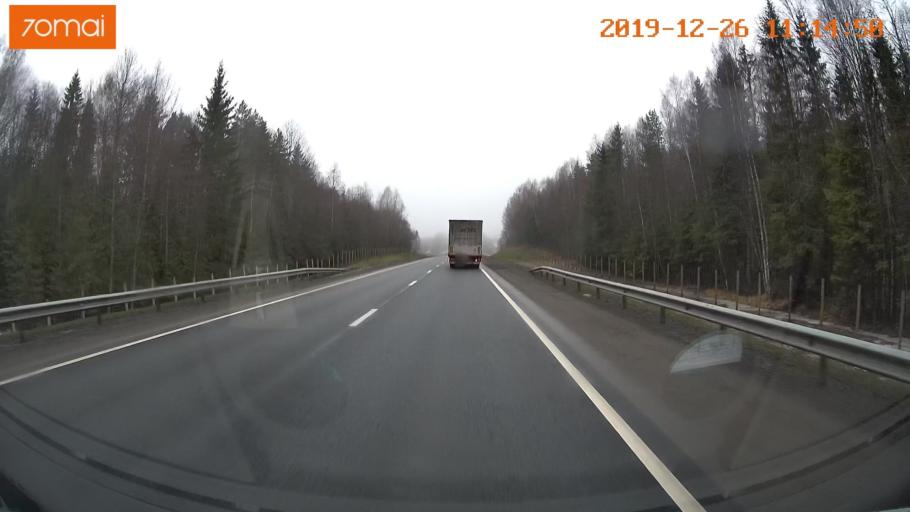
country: RU
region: Vologda
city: Chebsara
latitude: 59.1208
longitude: 39.1163
